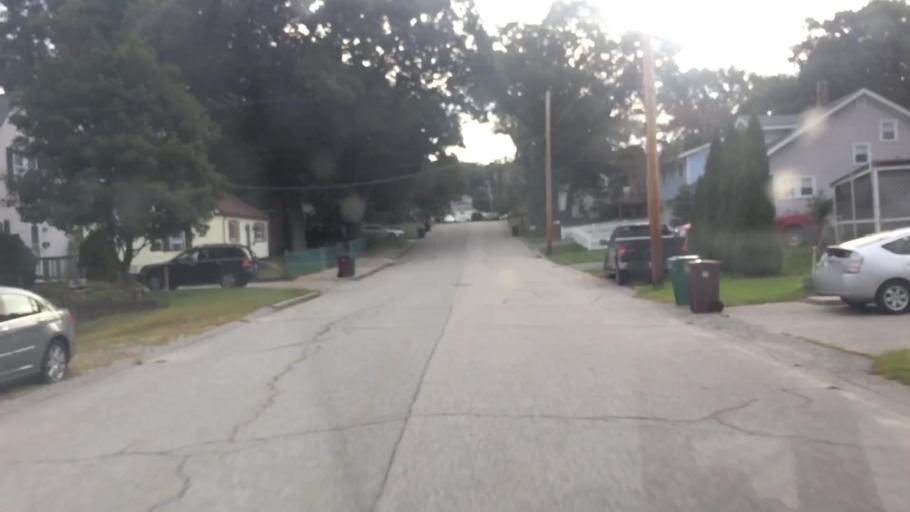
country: US
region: Rhode Island
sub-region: Providence County
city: Cumberland Hill
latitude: 41.9871
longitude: -71.4870
